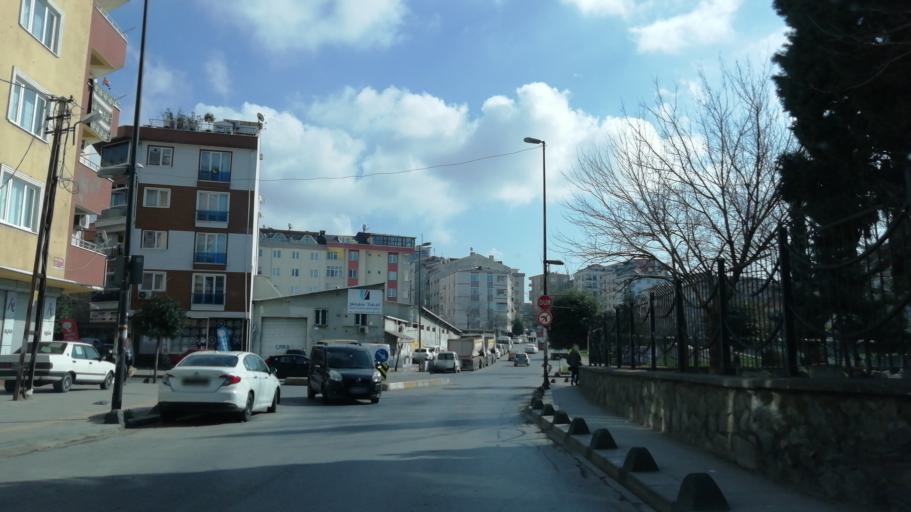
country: TR
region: Istanbul
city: Bahcelievler
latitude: 41.0156
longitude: 28.8389
